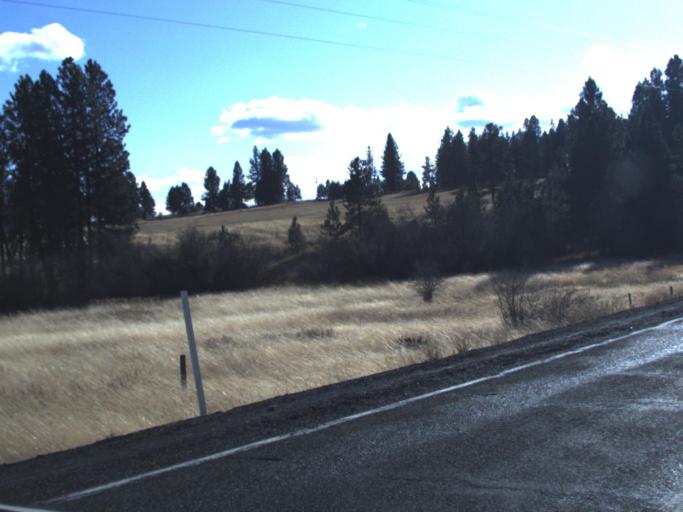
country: US
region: Washington
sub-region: Asotin County
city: Asotin
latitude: 46.1091
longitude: -117.1385
